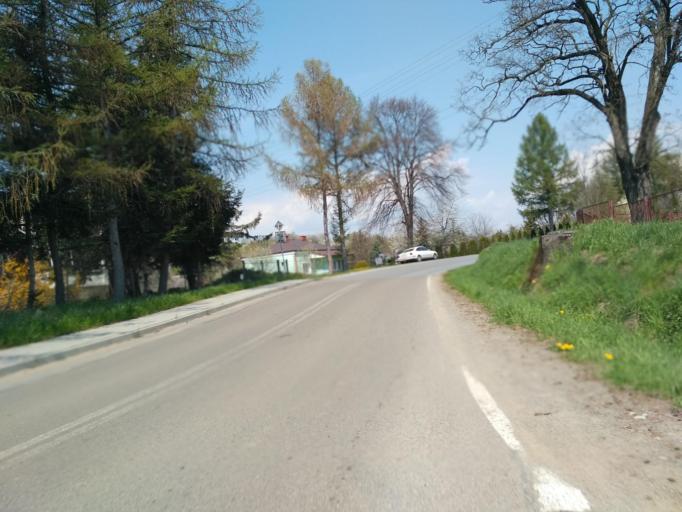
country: PL
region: Subcarpathian Voivodeship
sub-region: Powiat krosnienski
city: Chorkowka
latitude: 49.6455
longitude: 21.6710
